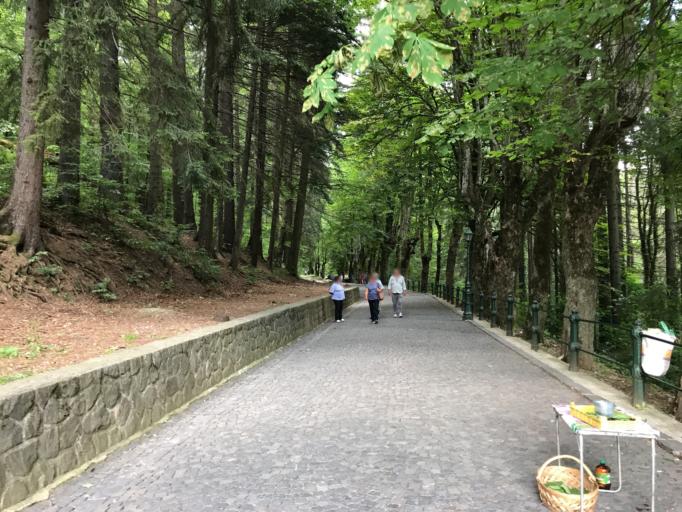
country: RO
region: Prahova
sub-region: Oras Sinaia
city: Sinaia
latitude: 45.3561
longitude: 25.5485
